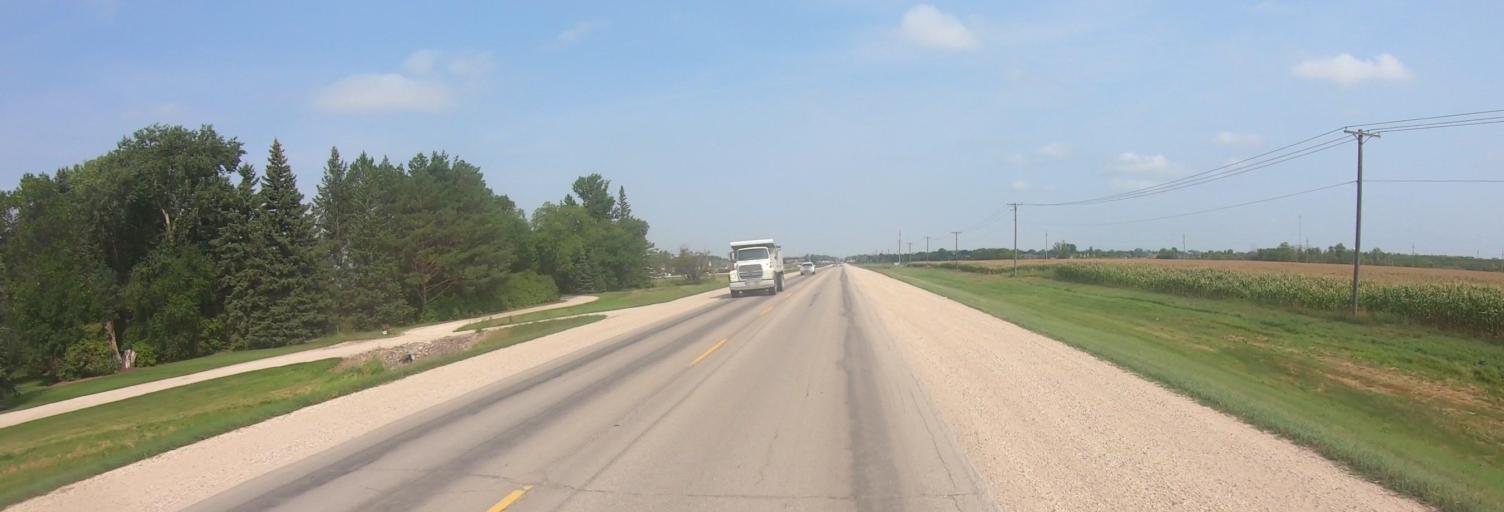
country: CA
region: Manitoba
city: Steinbach
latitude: 49.4993
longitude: -96.6912
